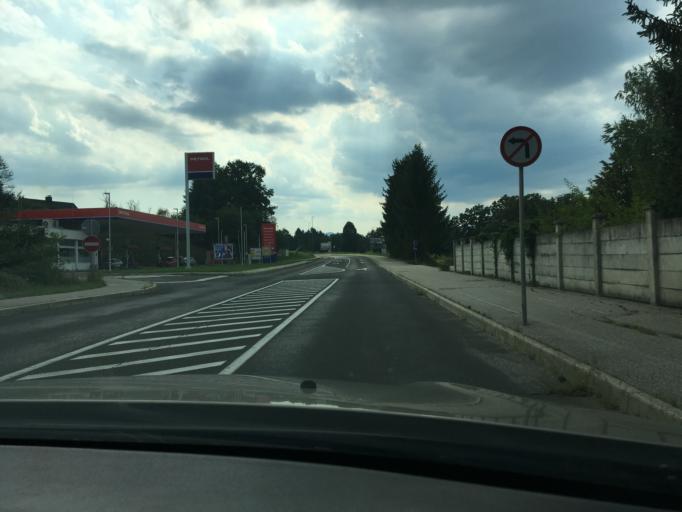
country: SI
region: Novo Mesto
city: Novo Mesto
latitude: 45.7992
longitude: 15.1512
